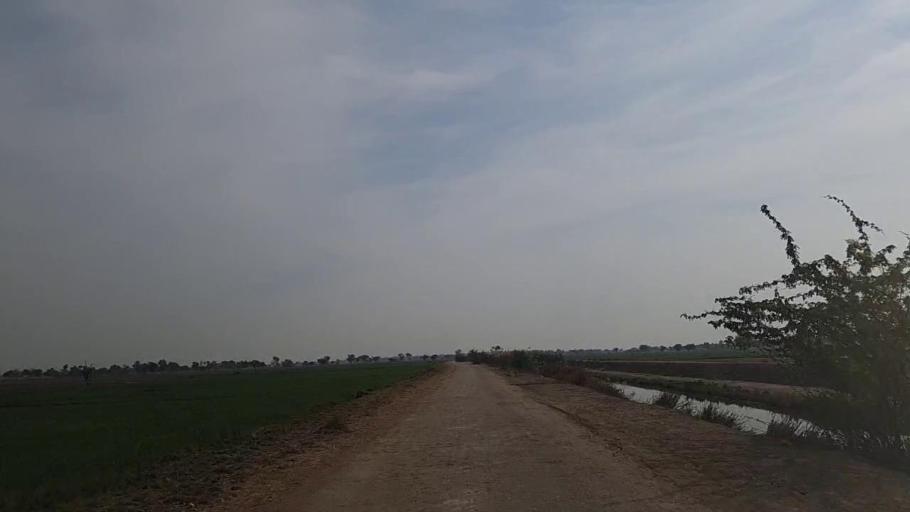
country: PK
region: Sindh
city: Daur
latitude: 26.4428
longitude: 68.4224
